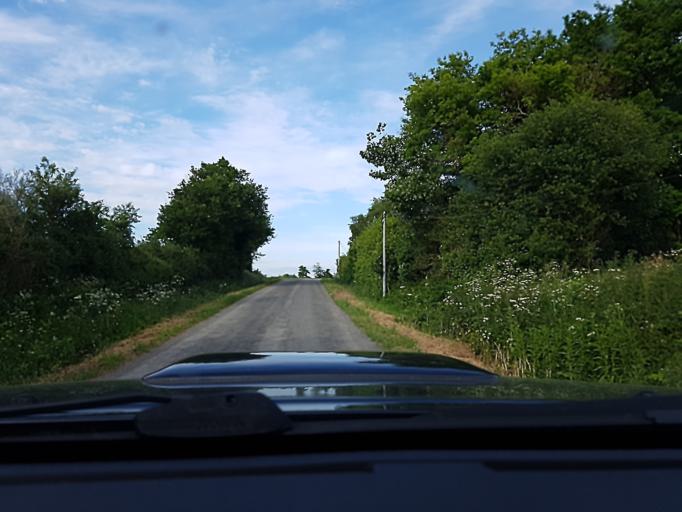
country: FR
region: Pays de la Loire
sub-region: Departement de la Vendee
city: Mache
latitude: 46.7629
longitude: -1.6654
